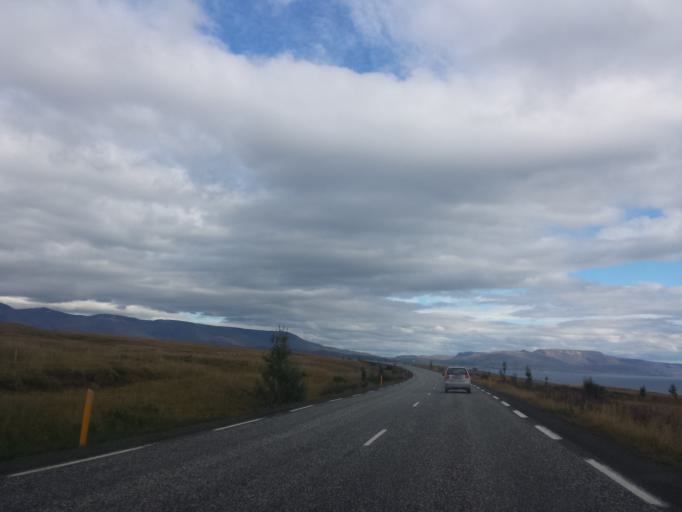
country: IS
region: Capital Region
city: Mosfellsbaer
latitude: 64.3390
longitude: -21.8272
